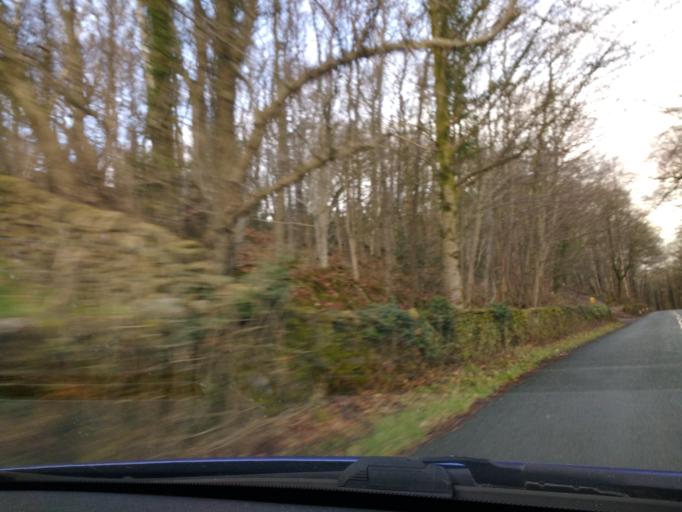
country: GB
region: England
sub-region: Lancashire
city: Caton
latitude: 54.0492
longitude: -2.7462
